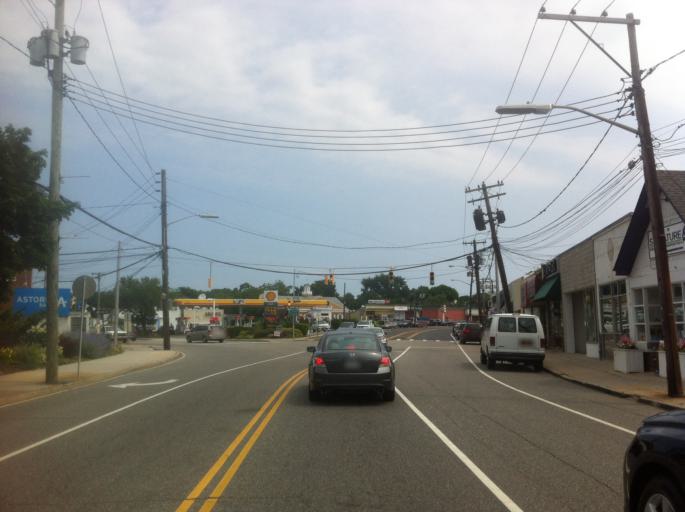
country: US
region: New York
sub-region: Nassau County
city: Syosset
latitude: 40.8249
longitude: -73.5021
